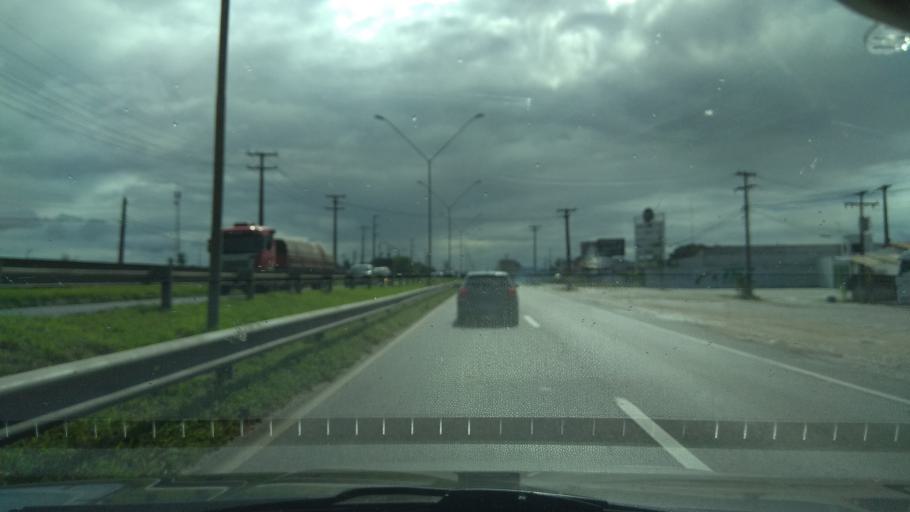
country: BR
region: Bahia
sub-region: Feira De Santana
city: Feira de Santana
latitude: -12.3110
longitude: -38.8844
